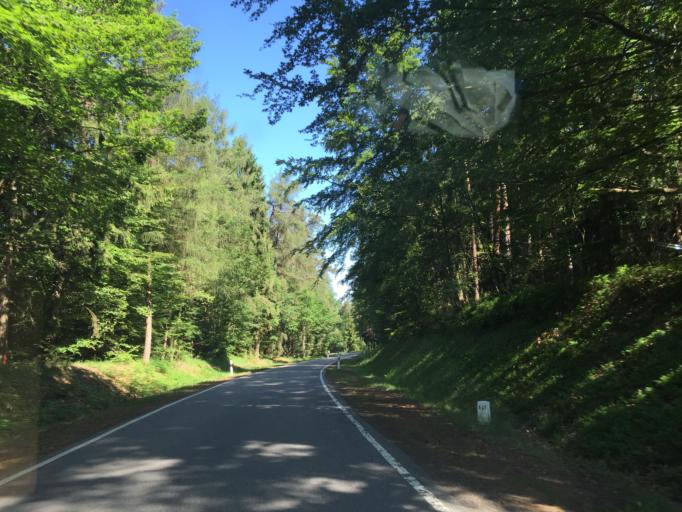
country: DE
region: Hesse
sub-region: Regierungsbezirk Darmstadt
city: Wald-Michelbach
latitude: 49.6010
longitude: 8.8997
